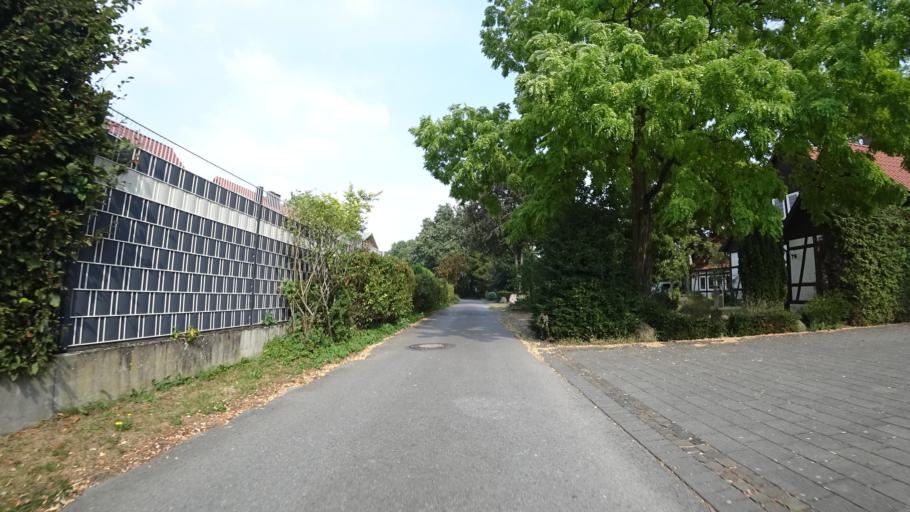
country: DE
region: North Rhine-Westphalia
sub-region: Regierungsbezirk Detmold
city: Guetersloh
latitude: 51.9274
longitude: 8.4421
